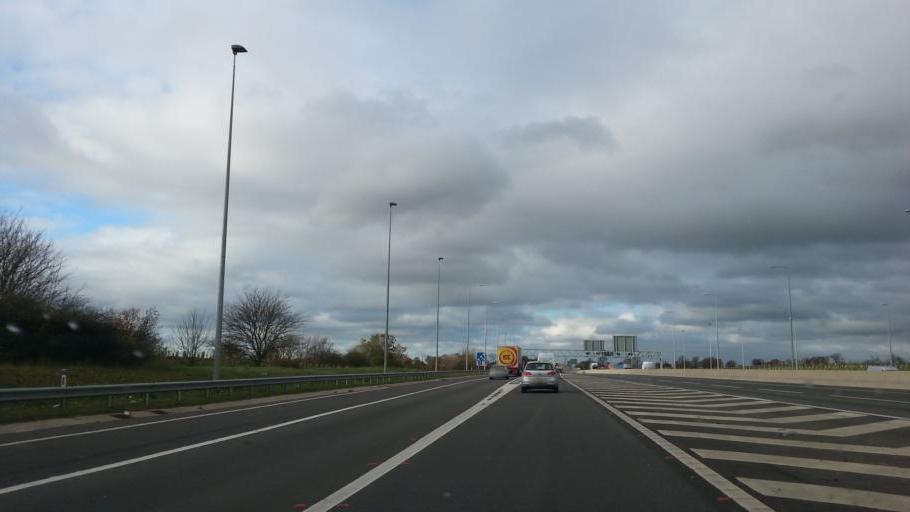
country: GB
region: England
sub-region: Leicestershire
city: Lutterworth
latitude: 52.4049
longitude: -1.1848
